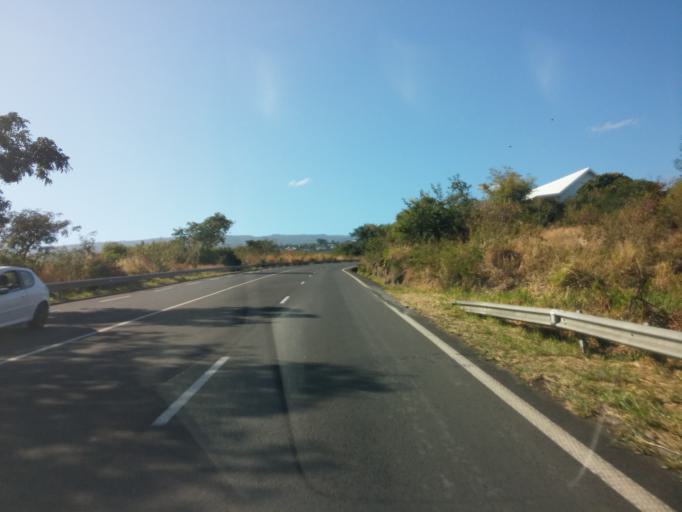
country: RE
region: Reunion
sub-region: Reunion
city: Saint-Paul
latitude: -21.0203
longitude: 55.2718
